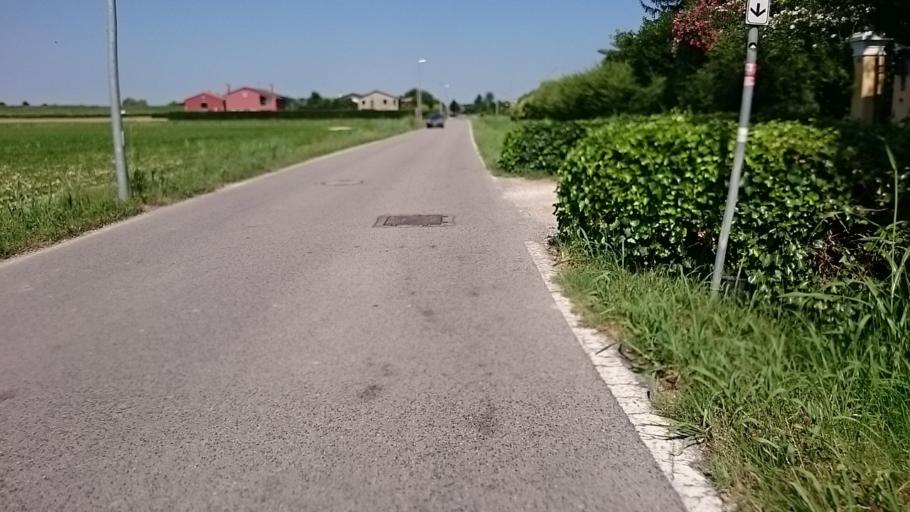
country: IT
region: Veneto
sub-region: Provincia di Venezia
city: Fosso
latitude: 45.3689
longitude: 12.0380
